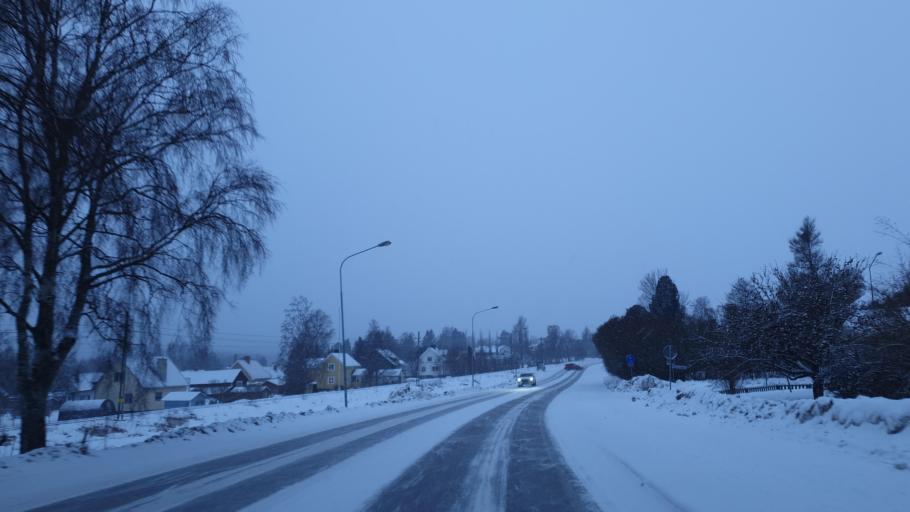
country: SE
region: Vaesternorrland
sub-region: OErnskoeldsviks Kommun
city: Ornskoldsvik
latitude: 63.2963
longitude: 18.6283
